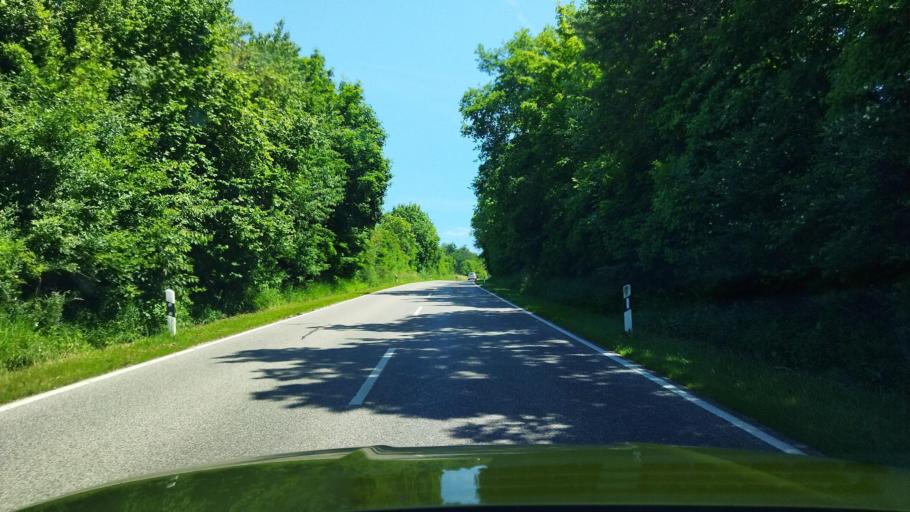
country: DE
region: Bavaria
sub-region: Upper Bavaria
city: Denkendorf
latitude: 48.9467
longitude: 11.5409
